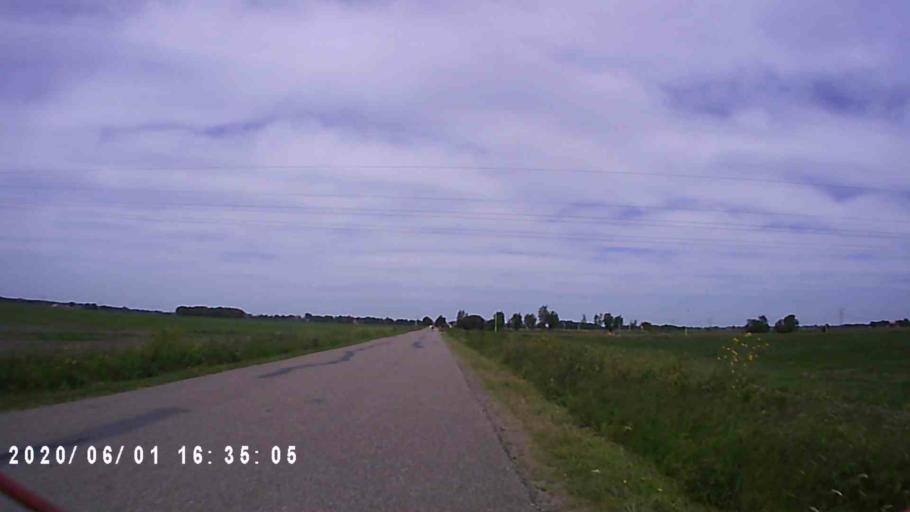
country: NL
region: Friesland
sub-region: Gemeente Leeuwarden
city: Camminghaburen
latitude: 53.1926
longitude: 5.8749
